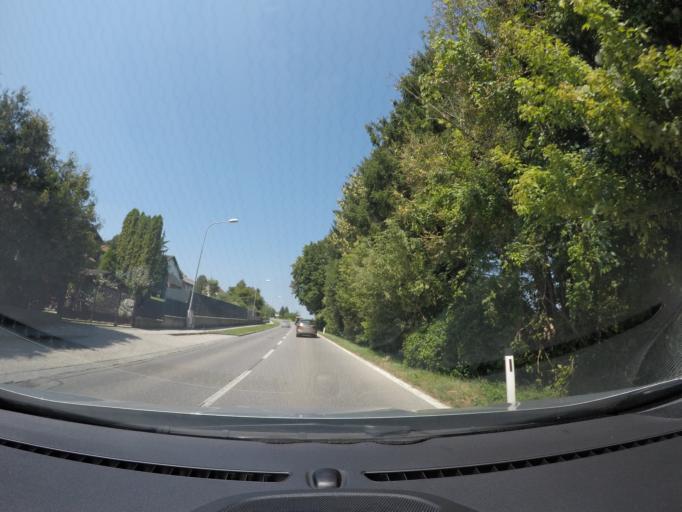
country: AT
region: Lower Austria
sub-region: Politischer Bezirk Sankt Polten
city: Maria-Anzbach
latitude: 48.1921
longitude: 15.9208
